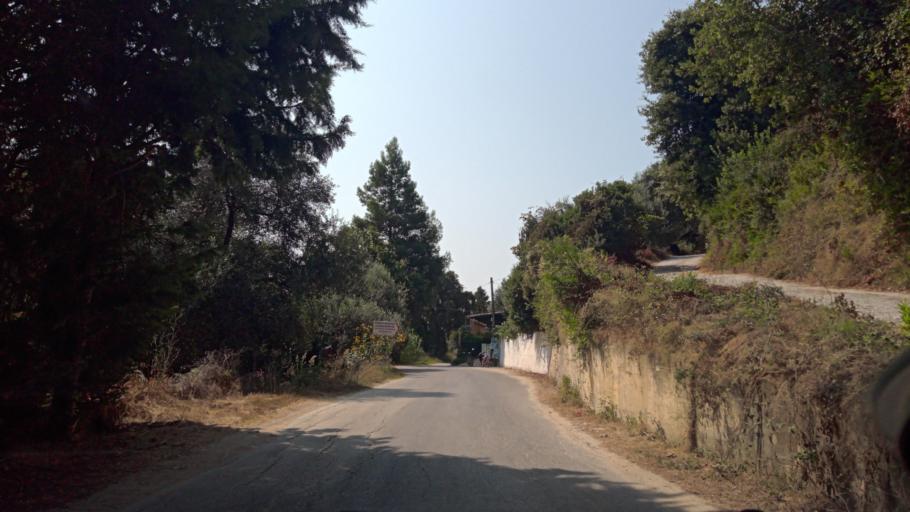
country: GR
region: Ionian Islands
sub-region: Nomos Kerkyras
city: Perivoli
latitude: 39.4000
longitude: 20.0246
